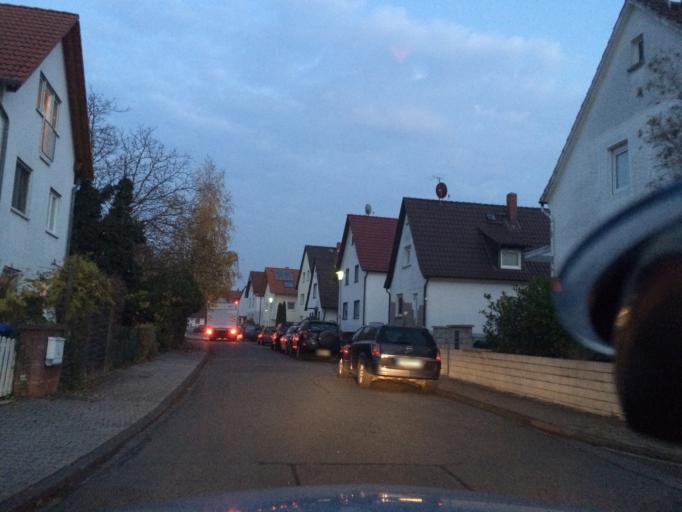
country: DE
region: Hesse
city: Morfelden-Walldorf
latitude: 49.9693
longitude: 8.5684
